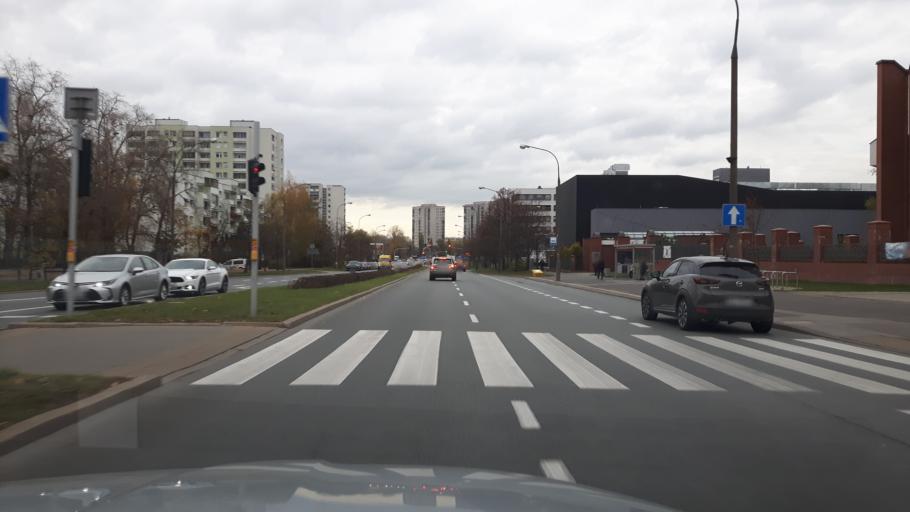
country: PL
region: Masovian Voivodeship
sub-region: Warszawa
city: Ursynow
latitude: 52.1478
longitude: 21.0425
